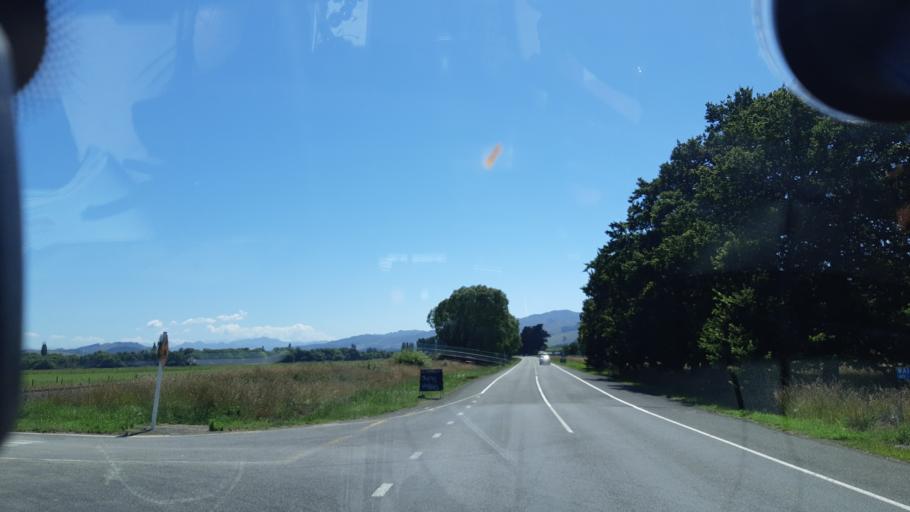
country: NZ
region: Canterbury
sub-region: Kaikoura District
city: Kaikoura
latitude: -42.7384
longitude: 173.2672
